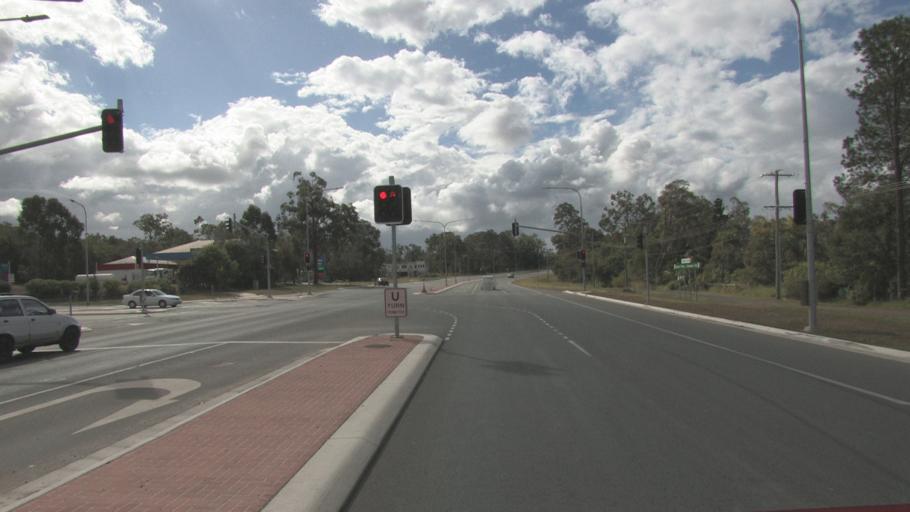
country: AU
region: Queensland
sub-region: Logan
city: Logan Reserve
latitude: -27.7092
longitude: 153.0937
